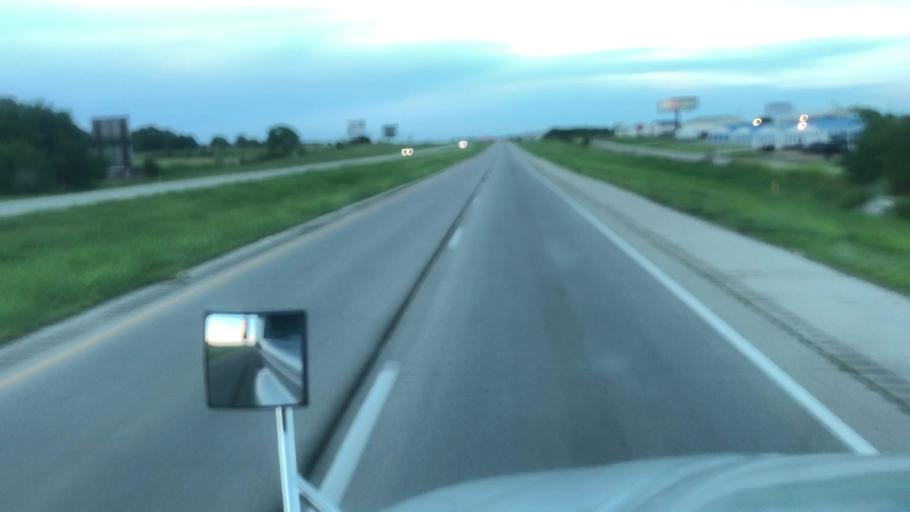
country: US
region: Oklahoma
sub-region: Kay County
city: Ponca City
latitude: 36.7558
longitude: -97.0651
